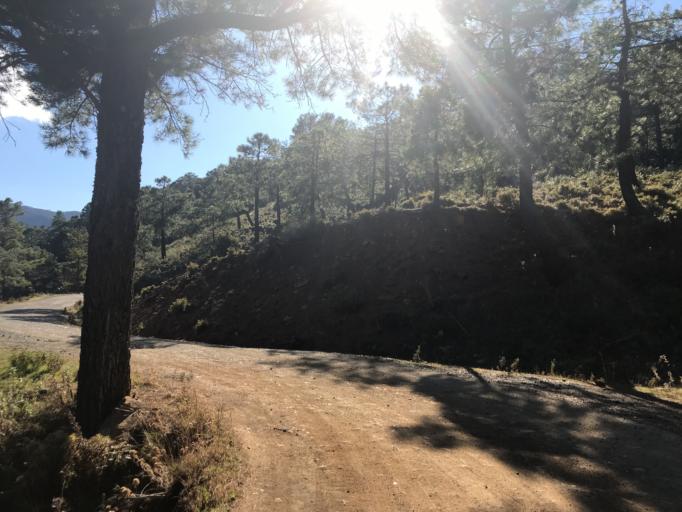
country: ES
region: Andalusia
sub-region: Provincia de Malaga
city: Tolox
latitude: 36.6794
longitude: -4.9262
